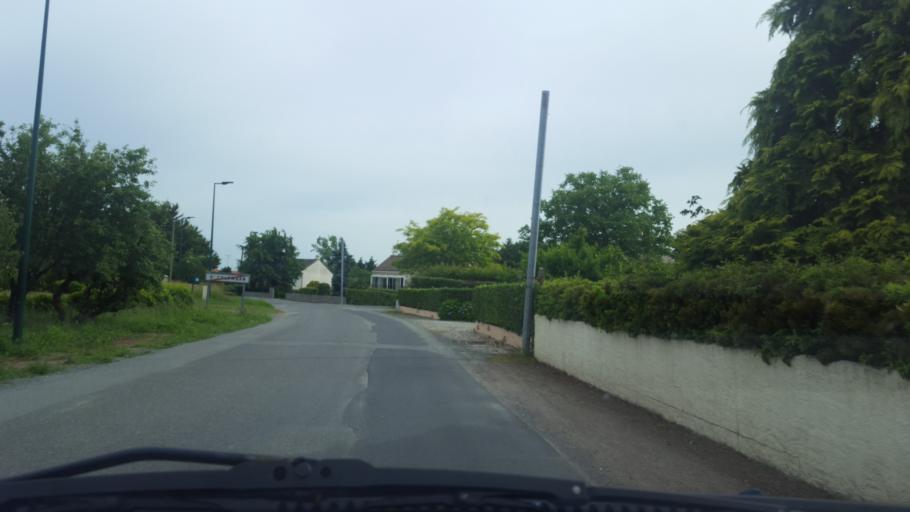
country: FR
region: Pays de la Loire
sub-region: Departement de la Loire-Atlantique
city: La Limouziniere
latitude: 47.0037
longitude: -1.5842
